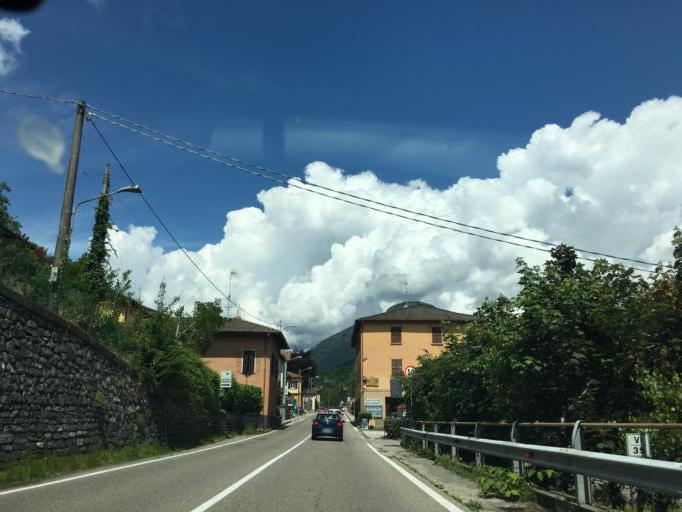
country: IT
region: Lombardy
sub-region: Provincia di Como
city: Grandola ed Uniti
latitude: 46.0225
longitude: 9.2148
